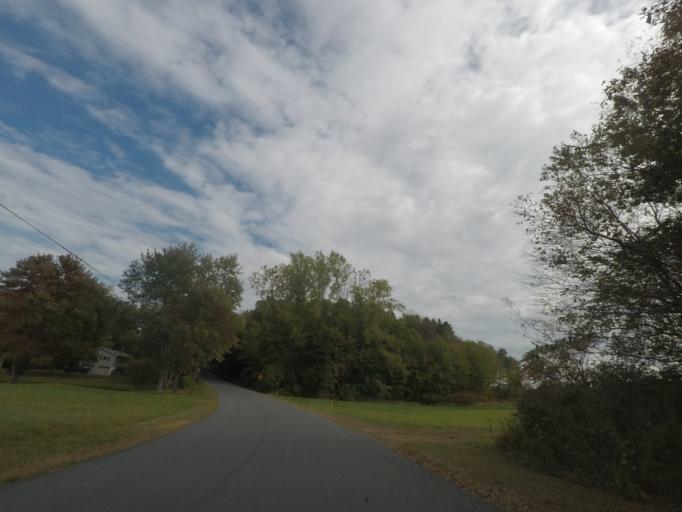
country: US
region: New York
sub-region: Rensselaer County
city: Nassau
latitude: 42.5470
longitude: -73.6334
